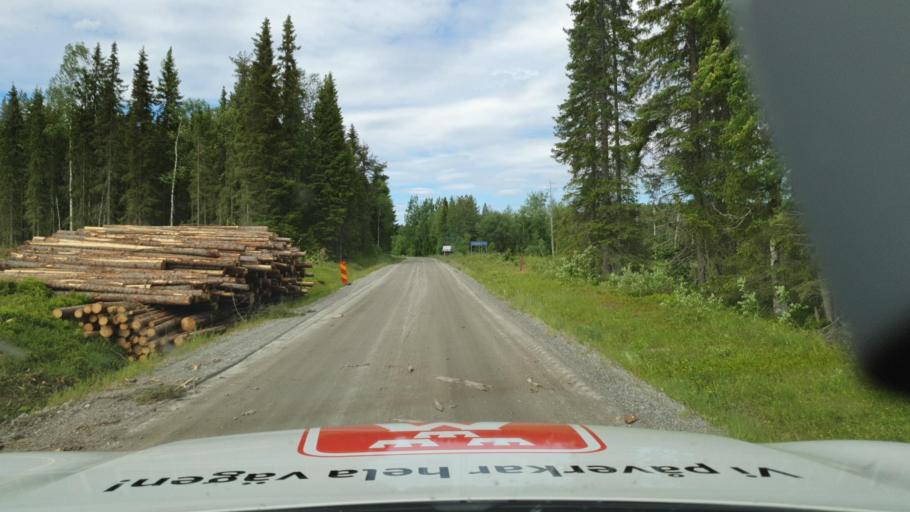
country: SE
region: Vaesterbotten
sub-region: Norsjo Kommun
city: Norsjoe
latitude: 64.7945
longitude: 19.6674
